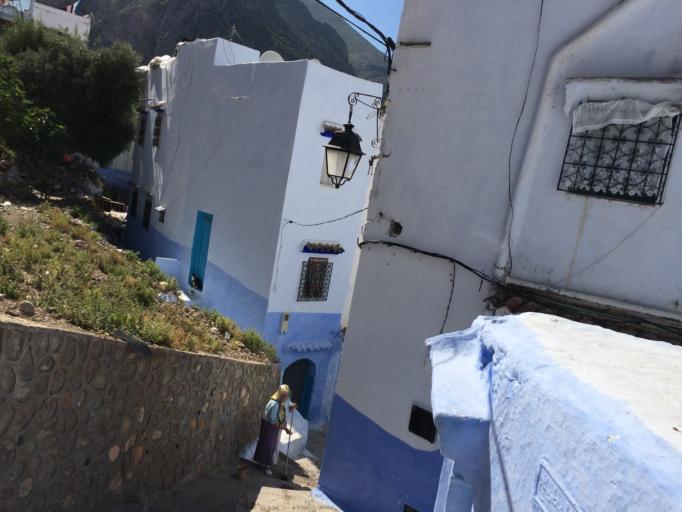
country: MA
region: Tanger-Tetouan
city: Chefchaouene
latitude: 35.1710
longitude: -5.2611
